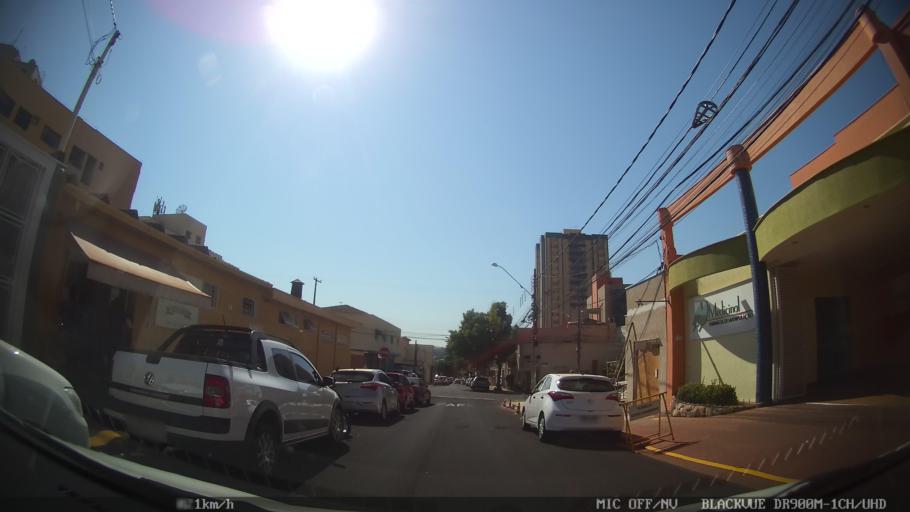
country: BR
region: Sao Paulo
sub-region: Ribeirao Preto
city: Ribeirao Preto
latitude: -21.1863
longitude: -47.8044
